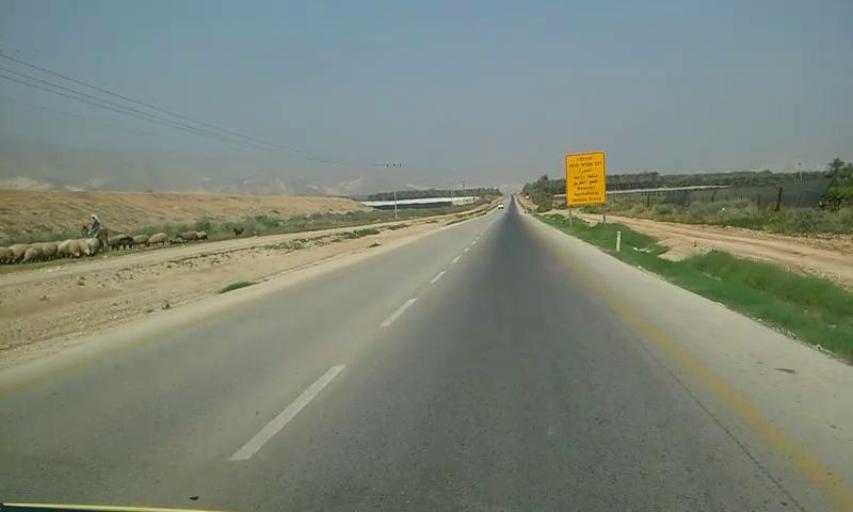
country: PS
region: West Bank
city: Al `Awja
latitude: 31.9889
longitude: 35.4605
